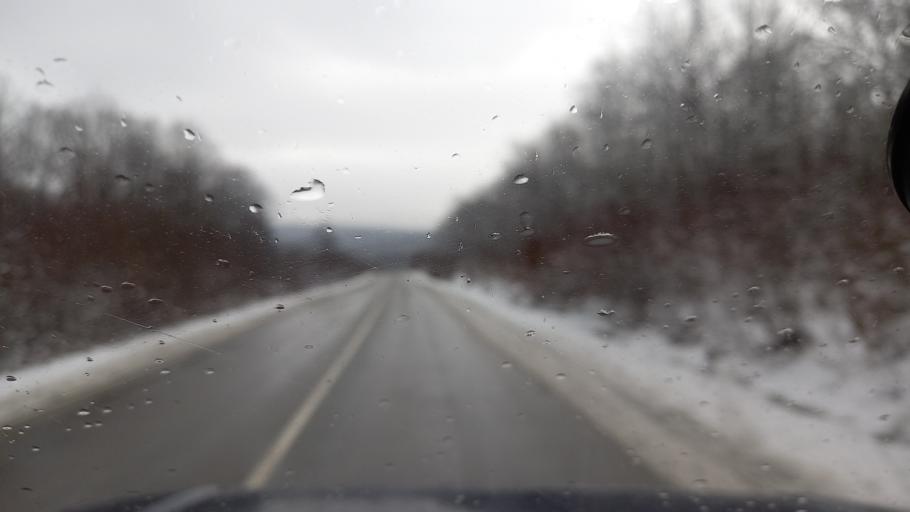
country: RU
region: Adygeya
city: Abadzekhskaya
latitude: 44.3798
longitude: 40.2410
